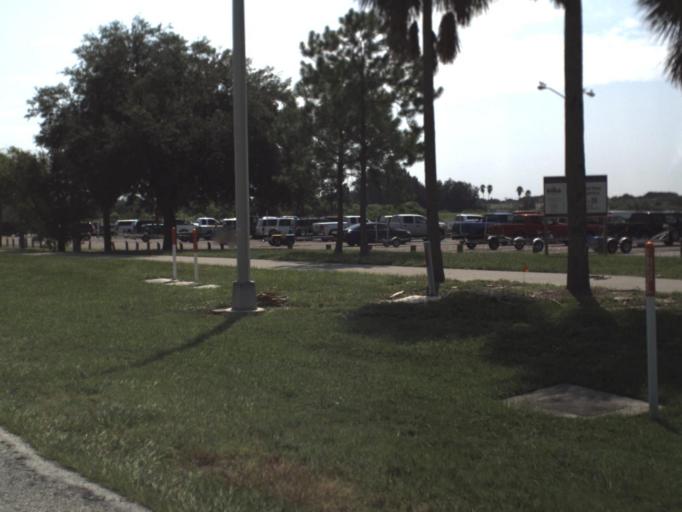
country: US
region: Florida
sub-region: Pinellas County
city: Gandy
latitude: 27.8932
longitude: -82.5330
